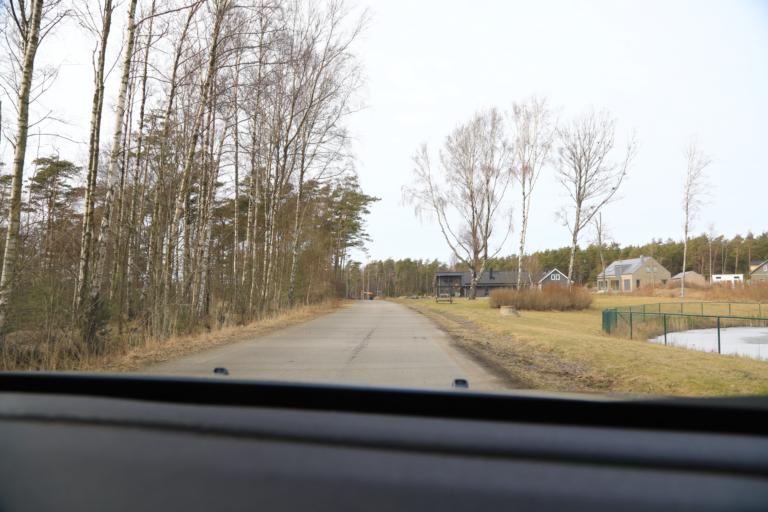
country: SE
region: Halland
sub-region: Kungsbacka Kommun
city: Frillesas
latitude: 57.2309
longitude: 12.1163
